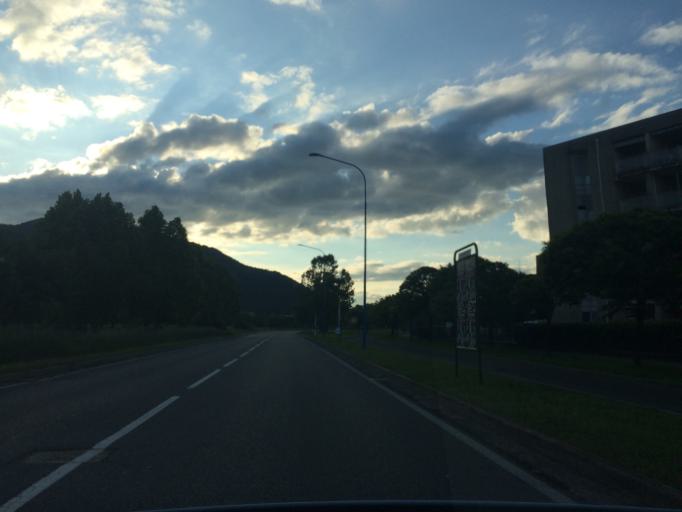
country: IT
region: Lombardy
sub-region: Provincia di Brescia
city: Buffalora-Bettole
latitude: 45.5237
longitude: 10.2578
